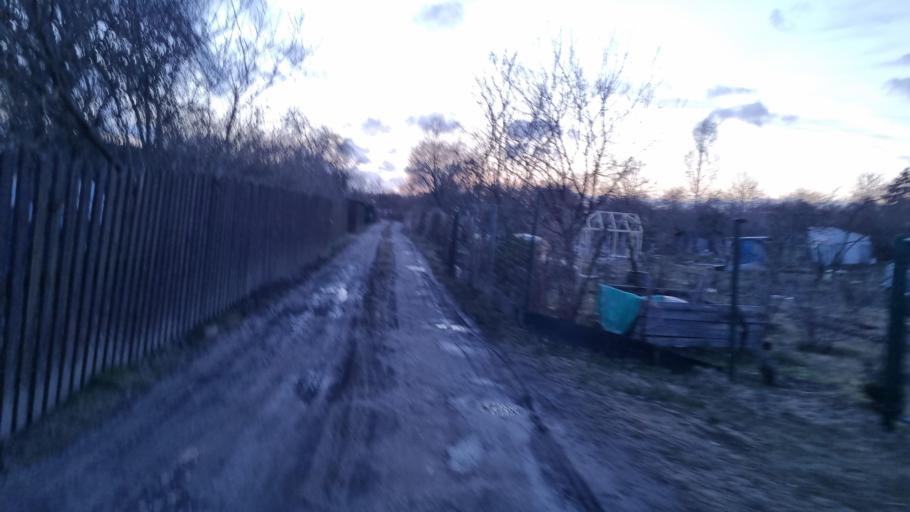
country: LV
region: Riga
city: Riga
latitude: 56.9196
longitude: 24.1287
